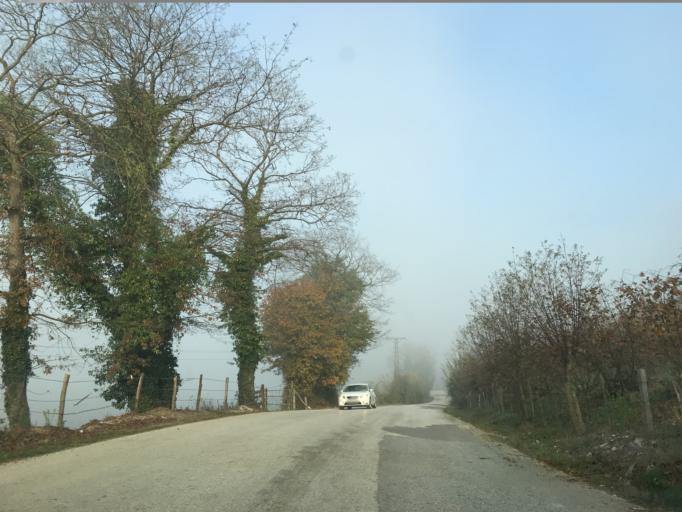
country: TR
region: Duzce
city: Cumayeri
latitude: 40.8976
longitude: 30.9520
